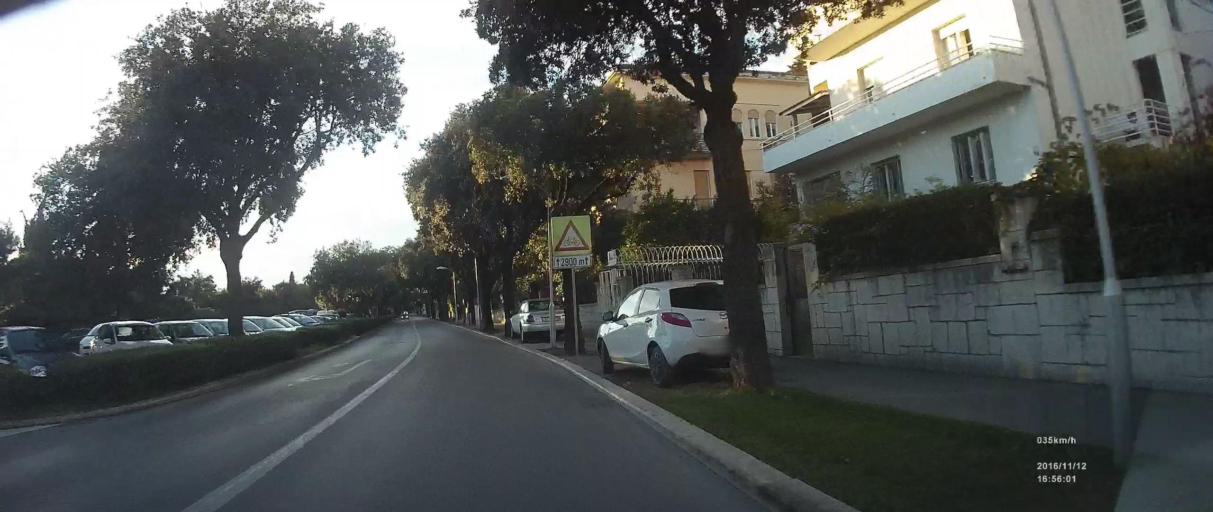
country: HR
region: Splitsko-Dalmatinska
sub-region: Grad Split
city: Split
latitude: 43.5034
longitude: 16.4264
